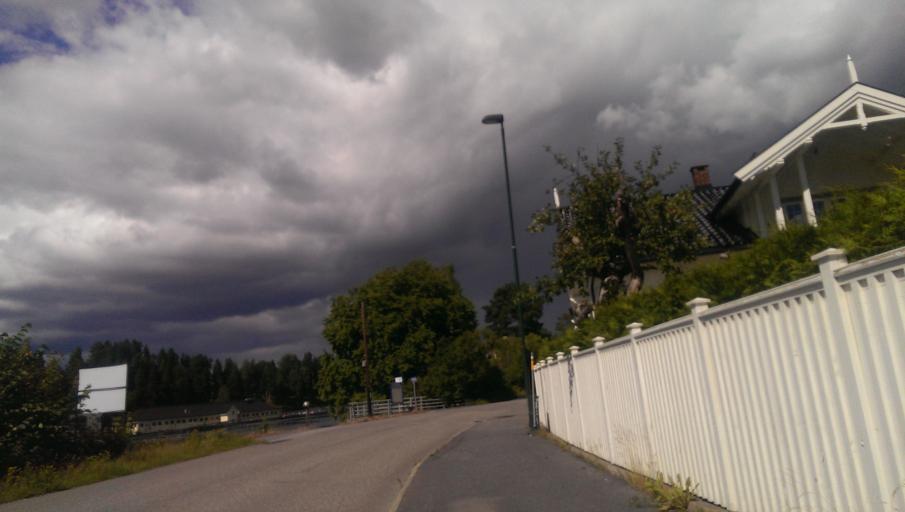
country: NO
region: Buskerud
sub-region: Kongsberg
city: Kongsberg
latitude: 59.6572
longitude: 9.6530
